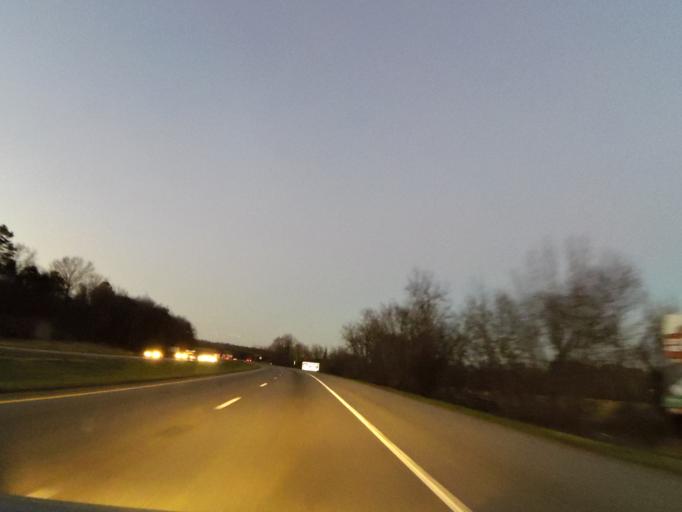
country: US
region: Tennessee
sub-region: Cocke County
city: Newport
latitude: 35.8979
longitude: -83.1843
